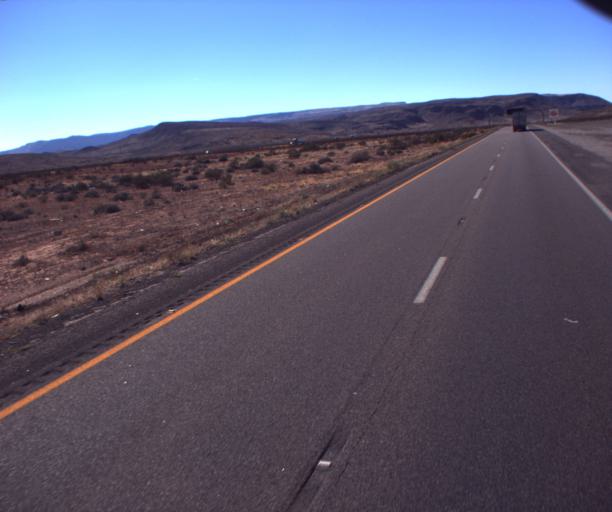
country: US
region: Utah
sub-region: Washington County
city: Saint George
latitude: 36.9882
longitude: -113.6321
